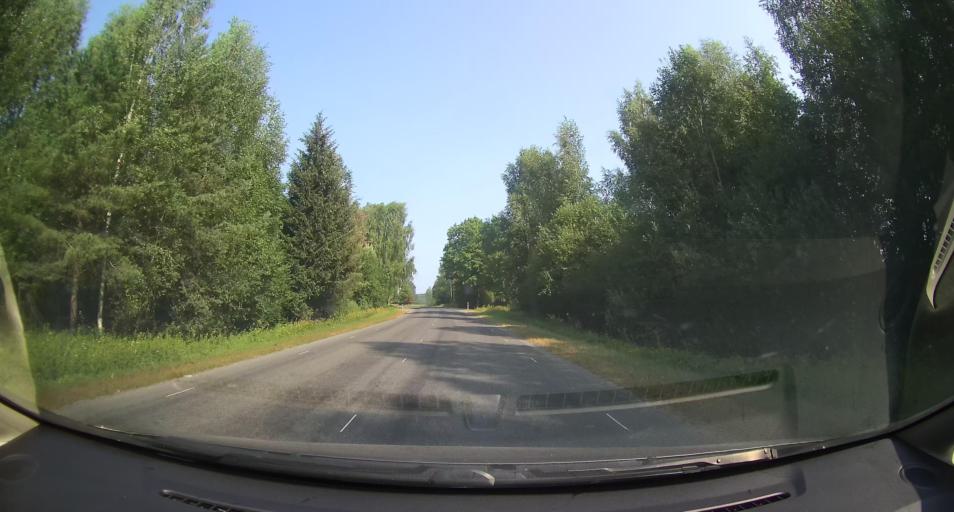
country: EE
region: Paernumaa
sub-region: Audru vald
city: Audru
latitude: 58.4290
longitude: 24.3153
